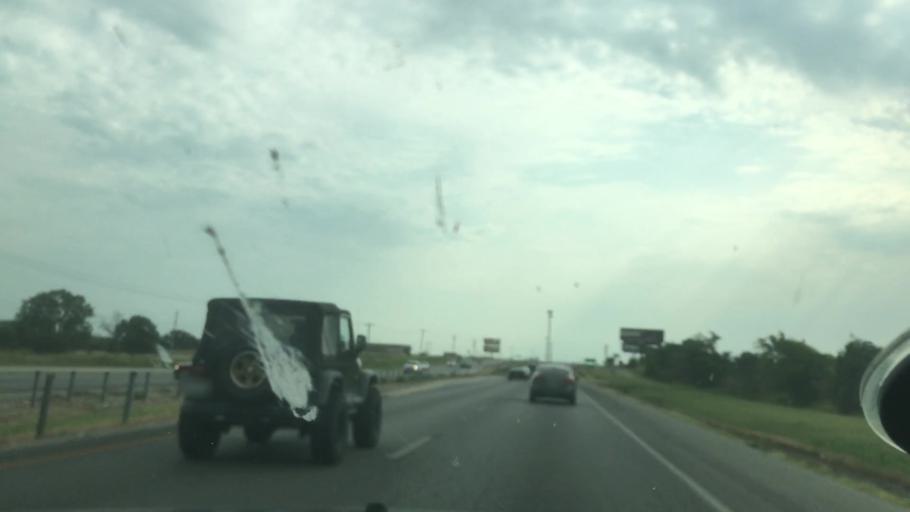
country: US
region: Oklahoma
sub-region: Bryan County
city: Calera
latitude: 33.9072
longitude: -96.4640
